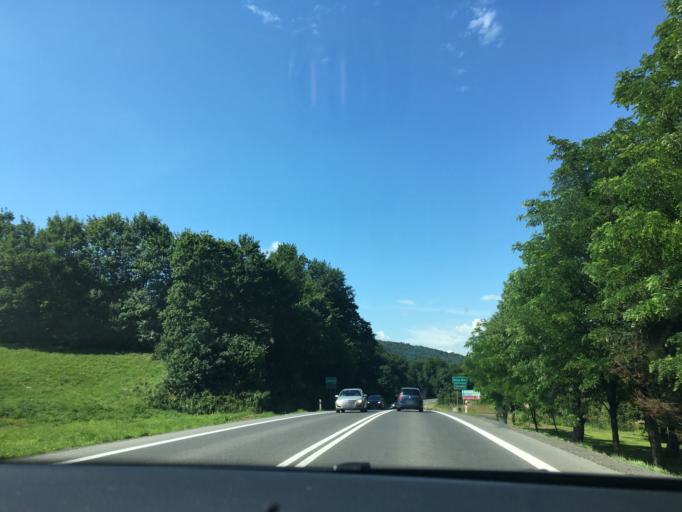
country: PL
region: Subcarpathian Voivodeship
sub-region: Powiat krosnienski
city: Dukla
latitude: 49.5144
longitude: 21.6942
